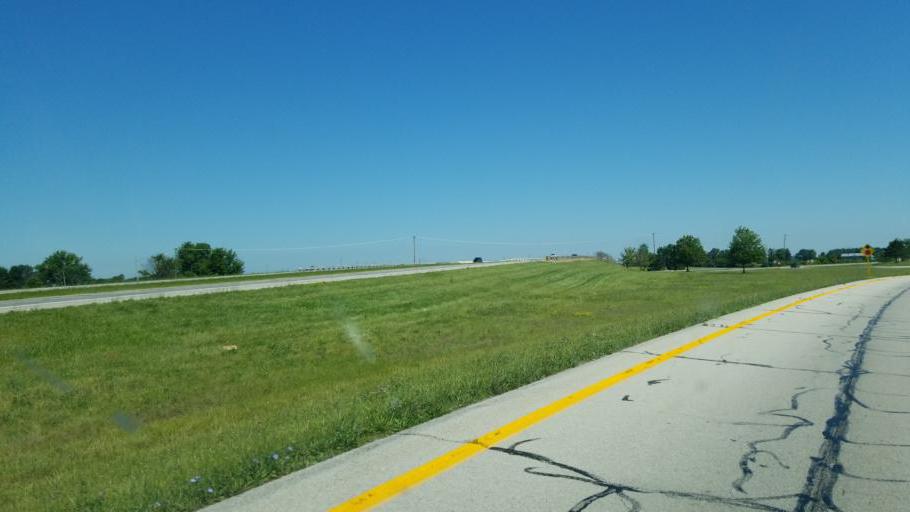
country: US
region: Ohio
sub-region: Marion County
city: Marion
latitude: 40.6624
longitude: -83.1092
